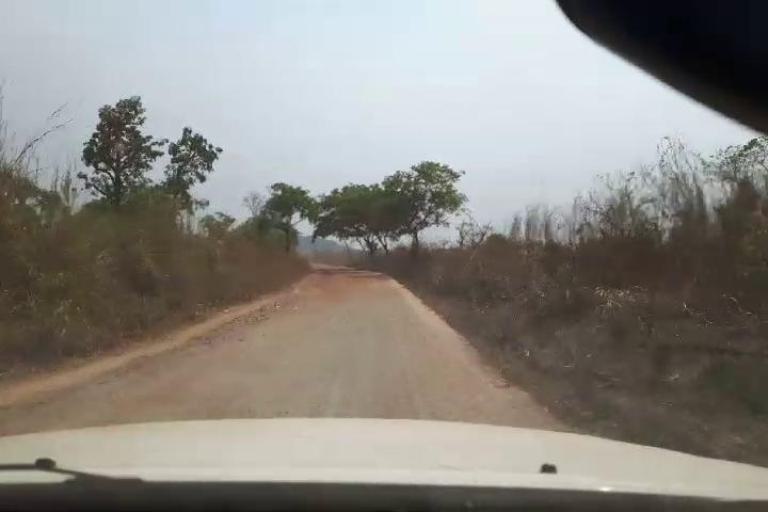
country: SL
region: Northern Province
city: Bumbuna
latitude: 9.0333
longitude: -11.7617
